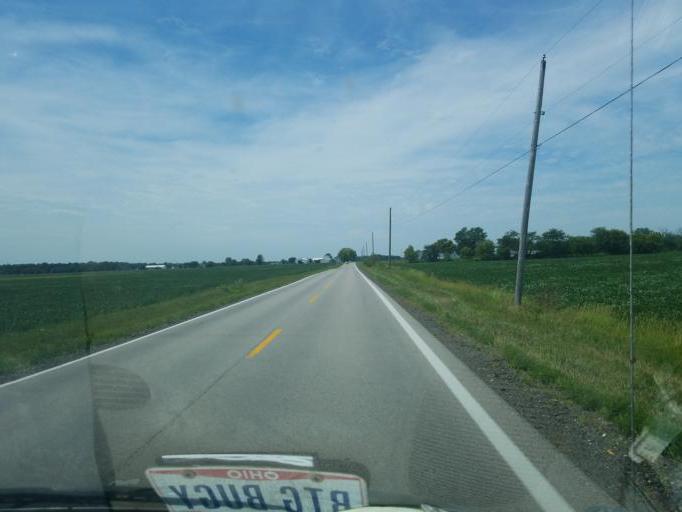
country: US
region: Ohio
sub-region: Madison County
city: West Jefferson
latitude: 39.8753
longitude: -83.3102
